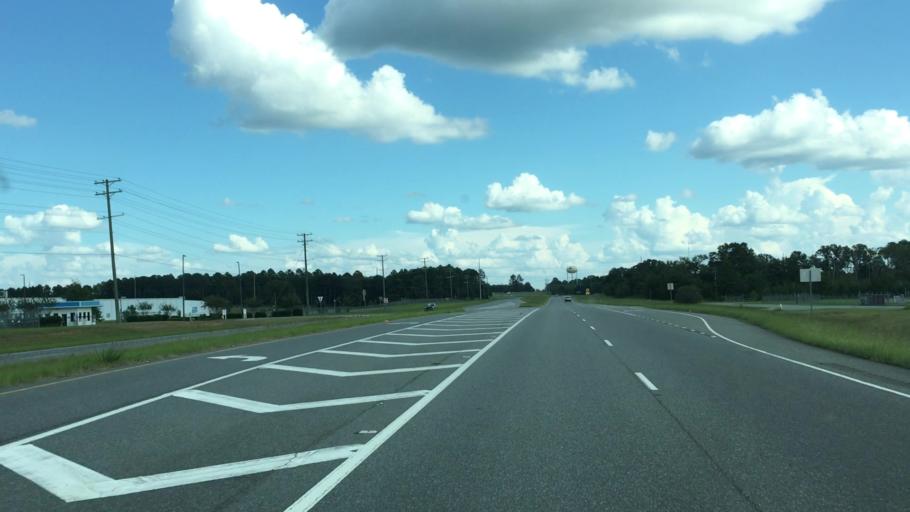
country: US
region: Georgia
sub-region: Laurens County
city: Dublin
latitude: 32.5080
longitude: -82.9477
